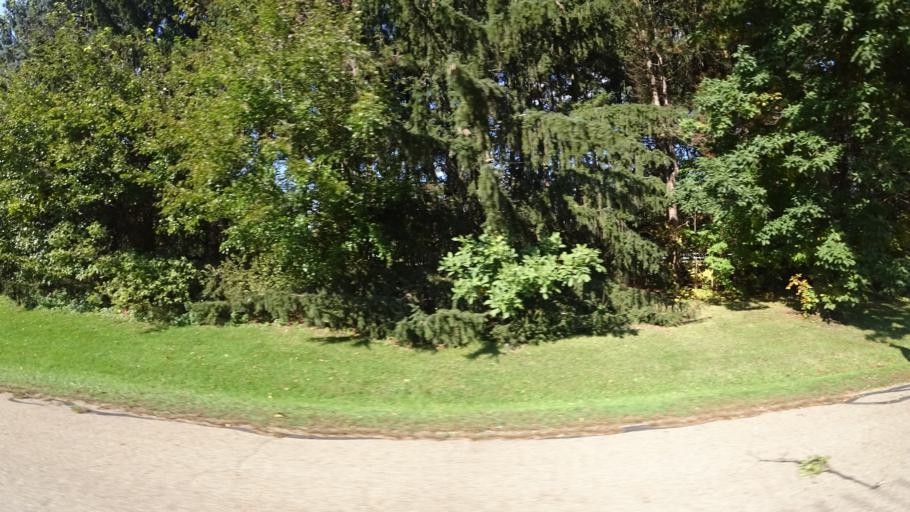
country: US
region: Michigan
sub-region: Calhoun County
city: Homer
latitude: 42.1492
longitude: -84.7967
